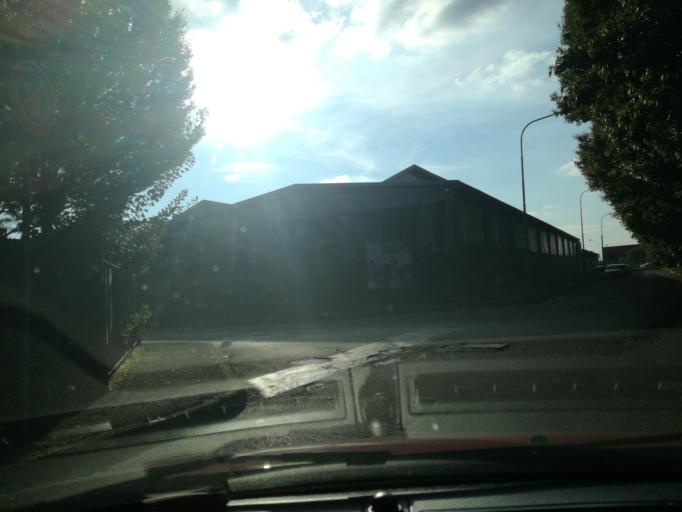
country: IT
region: Lombardy
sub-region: Provincia di Monza e Brianza
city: Vimercate
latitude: 45.6069
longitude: 9.3645
